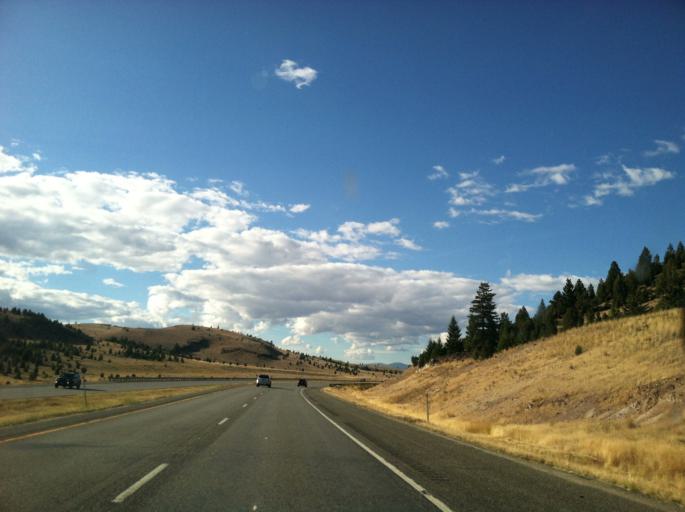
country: US
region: Montana
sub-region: Silver Bow County
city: Butte-Silver Bow (Balance)
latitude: 46.0225
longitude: -112.7253
